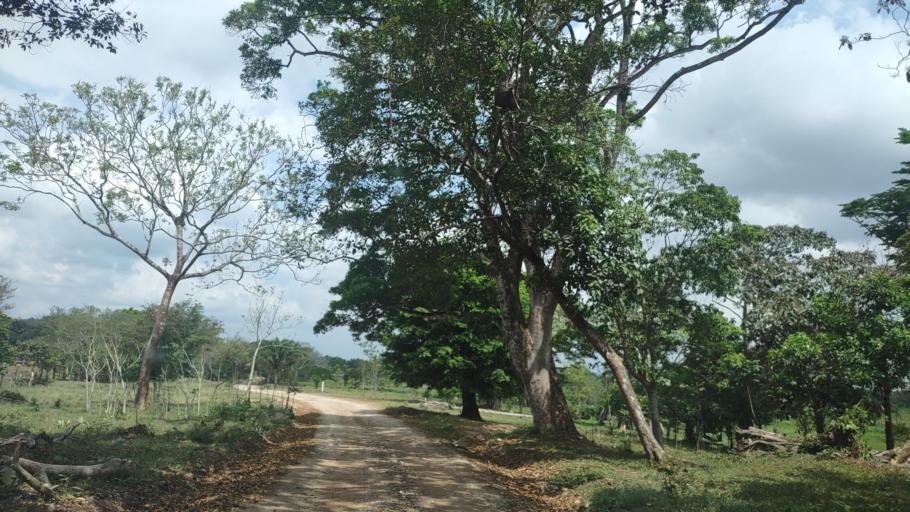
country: MX
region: Veracruz
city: Las Choapas
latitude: 17.9597
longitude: -94.1183
